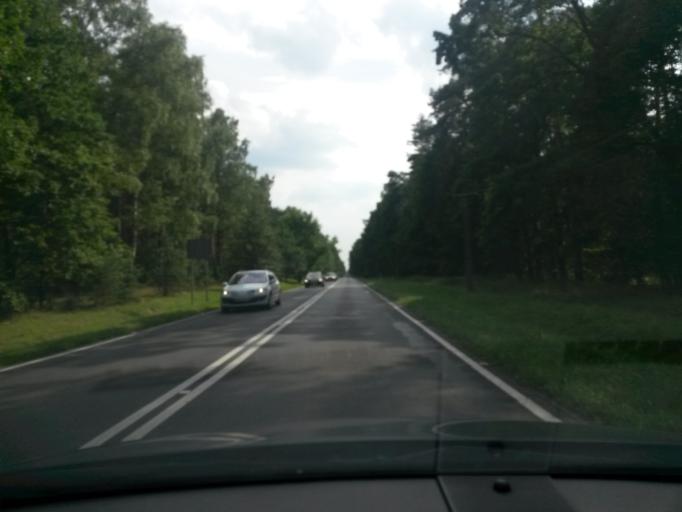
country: PL
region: Greater Poland Voivodeship
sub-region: Powiat poznanski
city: Kornik
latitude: 52.2161
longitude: 17.0724
